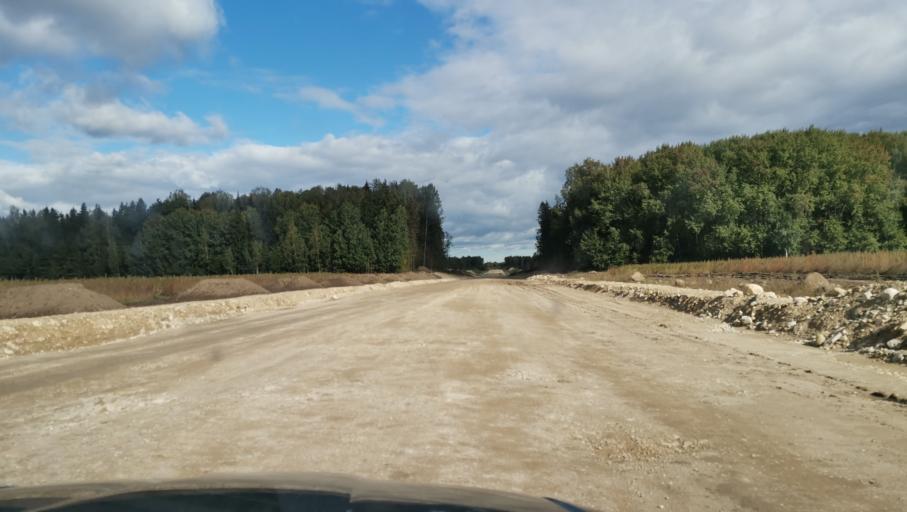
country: EE
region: Harju
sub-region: Nissi vald
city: Riisipere
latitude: 59.1380
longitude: 24.4863
